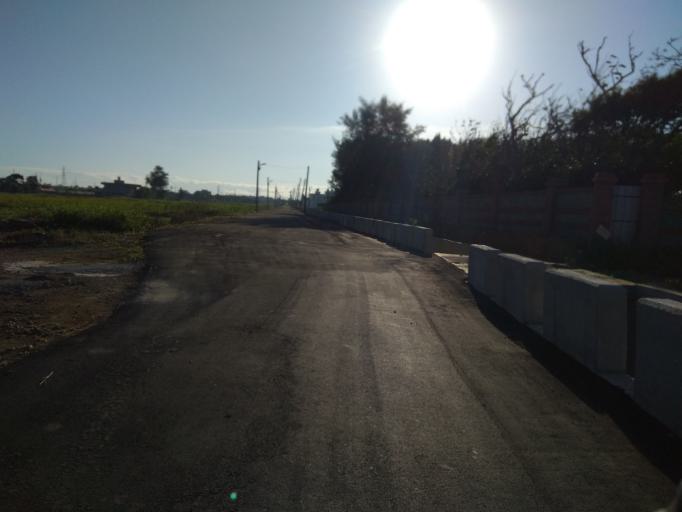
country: TW
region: Taiwan
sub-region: Hsinchu
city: Zhubei
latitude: 24.9883
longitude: 121.0470
